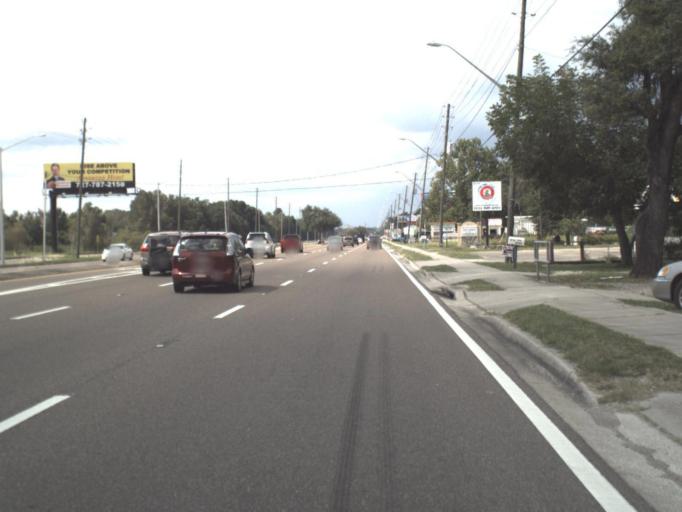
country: US
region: Florida
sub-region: Pasco County
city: Land O' Lakes
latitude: 28.1974
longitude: -82.4644
